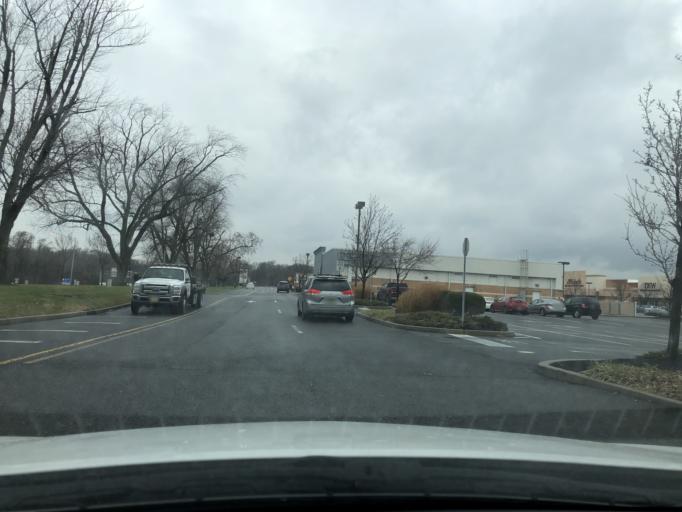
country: US
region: New Jersey
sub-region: Camden County
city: Glendora
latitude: 39.8396
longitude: -75.0919
